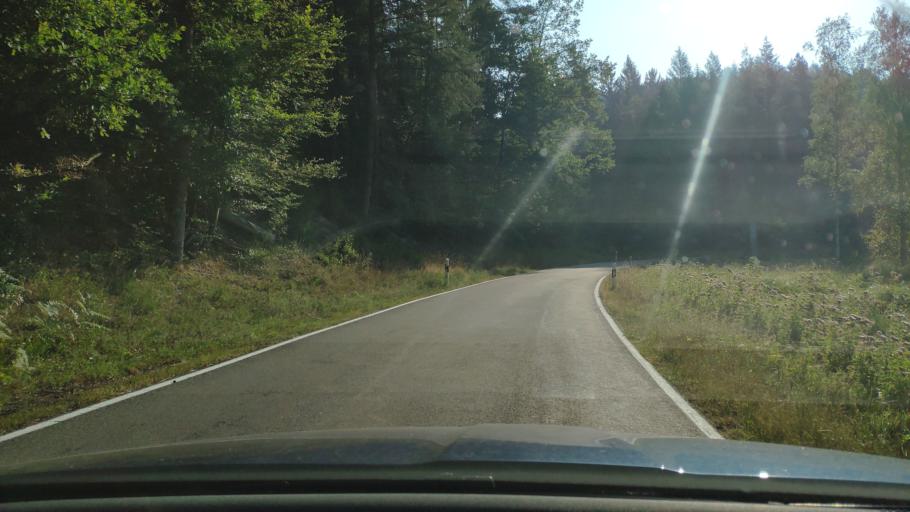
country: DE
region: Rheinland-Pfalz
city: Ludwigswinkel
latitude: 49.0905
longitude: 7.6491
